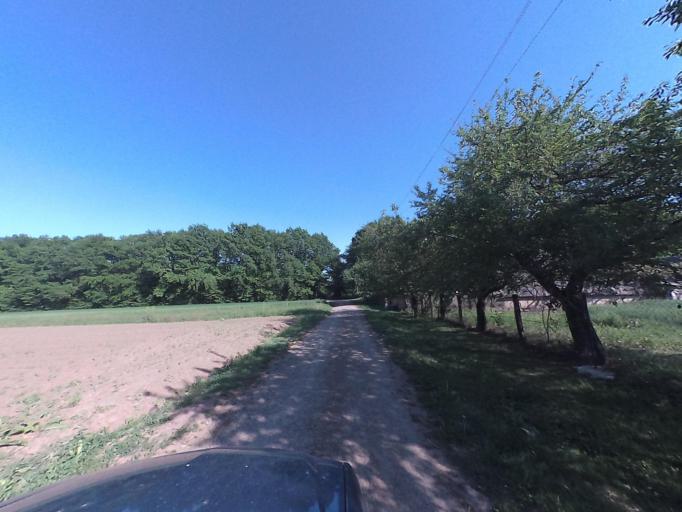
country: RO
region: Neamt
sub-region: Comuna Dulcesti
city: Dulcesti
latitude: 46.9970
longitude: 26.7829
